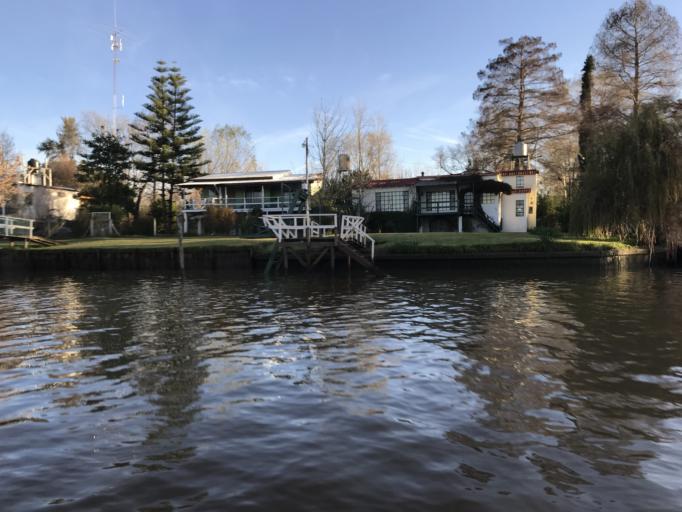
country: AR
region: Buenos Aires
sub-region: Partido de Tigre
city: Tigre
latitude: -34.3885
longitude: -58.5774
